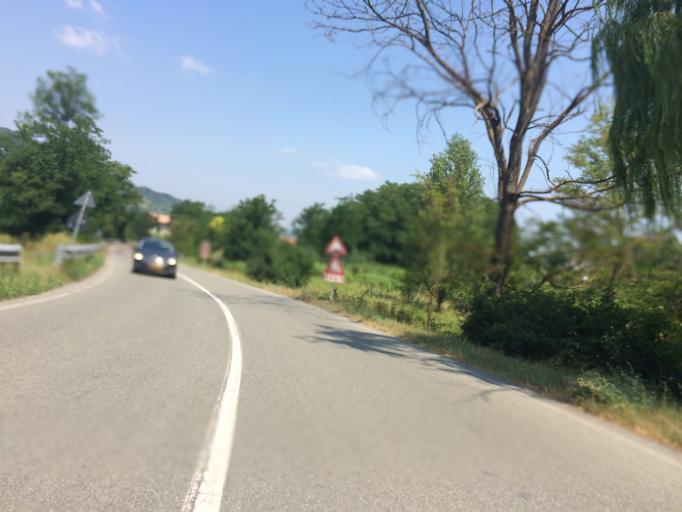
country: IT
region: Piedmont
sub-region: Provincia di Alessandria
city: Castelletto d'Erro
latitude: 44.6198
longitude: 8.4161
